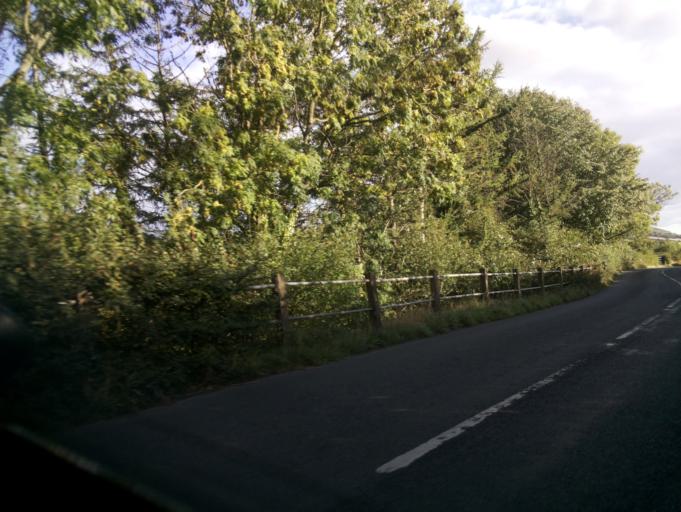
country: GB
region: England
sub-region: Devon
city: Sidmouth
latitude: 50.7113
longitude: -3.2242
